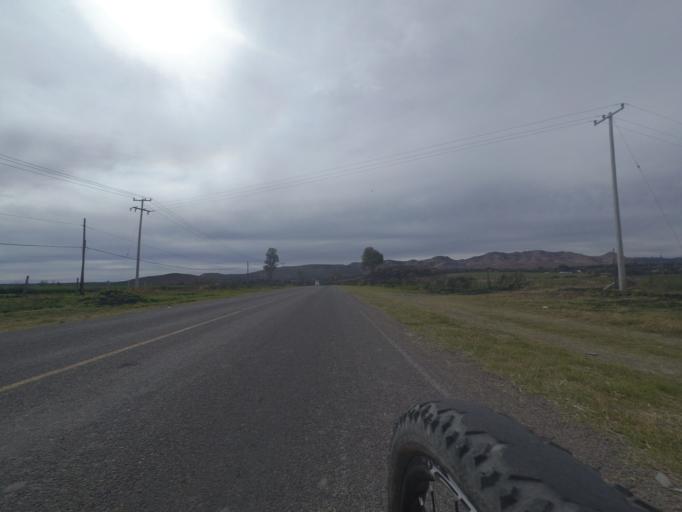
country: MX
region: Aguascalientes
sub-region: Aguascalientes
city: La Loma de los Negritos
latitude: 21.8370
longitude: -102.3604
